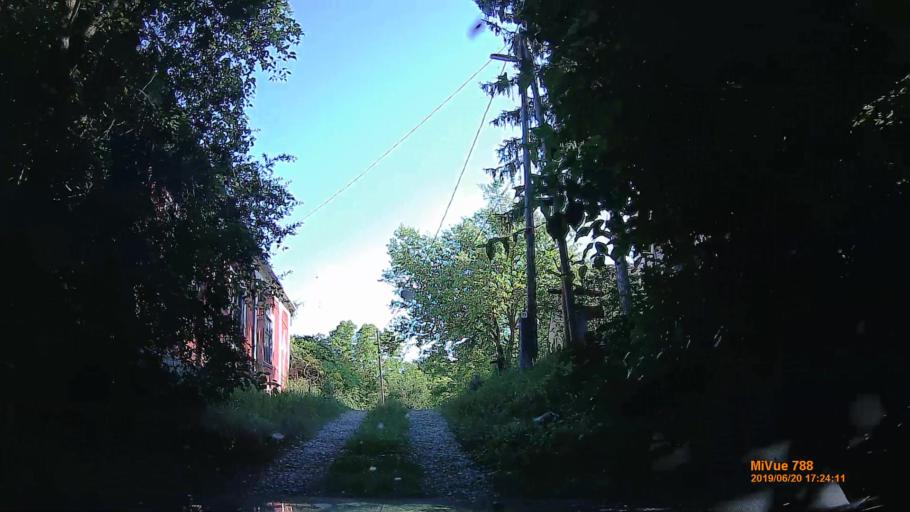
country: HU
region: Baranya
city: Buekkoesd
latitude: 46.1655
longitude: 18.0085
